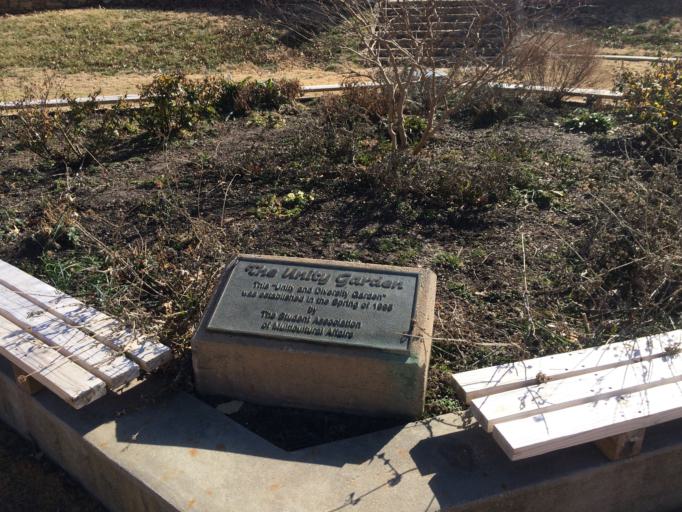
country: US
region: Oklahoma
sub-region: Cleveland County
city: Norman
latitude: 35.2049
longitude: -97.4456
